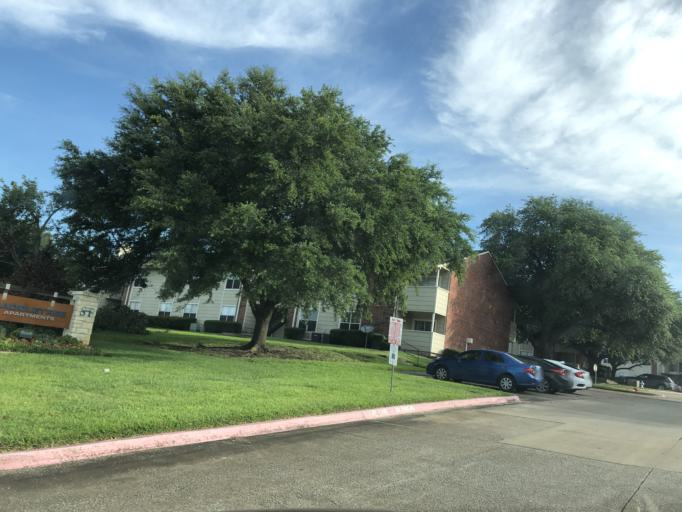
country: US
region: Texas
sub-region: Dallas County
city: Sunnyvale
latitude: 32.8481
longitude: -96.6041
